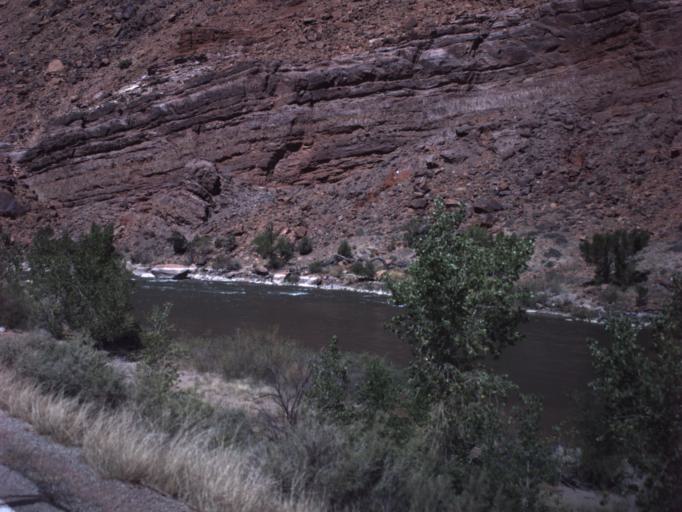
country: US
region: Utah
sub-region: Grand County
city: Moab
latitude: 38.6839
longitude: -109.4585
